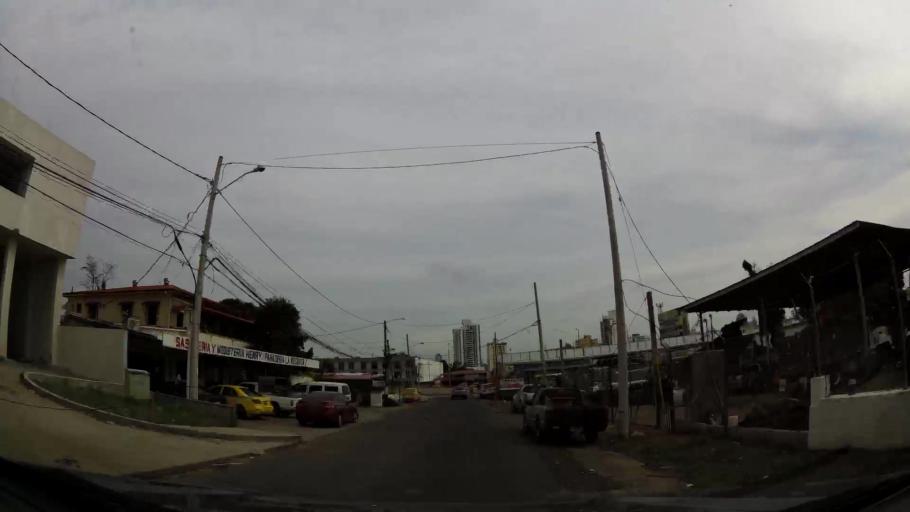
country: PA
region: Panama
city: Panama
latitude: 9.0088
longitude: -79.5195
